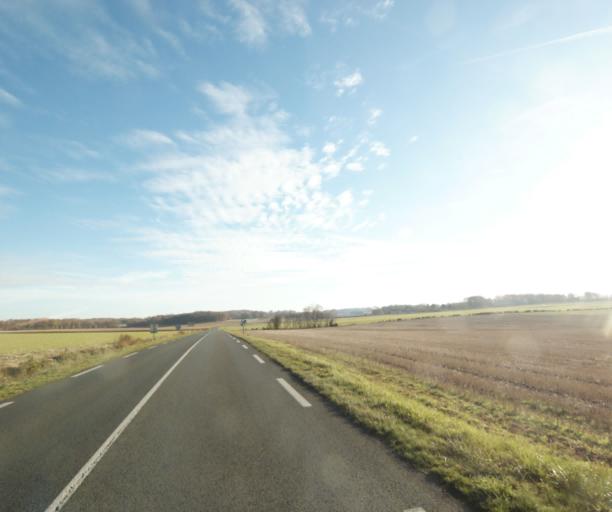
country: FR
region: Poitou-Charentes
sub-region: Departement de la Charente-Maritime
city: Saint-Georges-des-Coteaux
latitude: 45.7462
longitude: -0.7084
